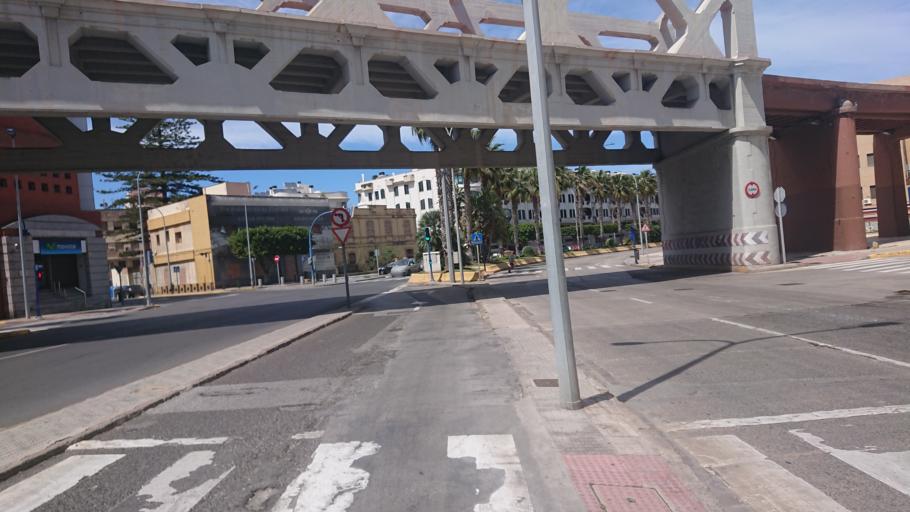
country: ES
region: Melilla
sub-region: Melilla
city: Melilla
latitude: 35.2894
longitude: -2.9397
